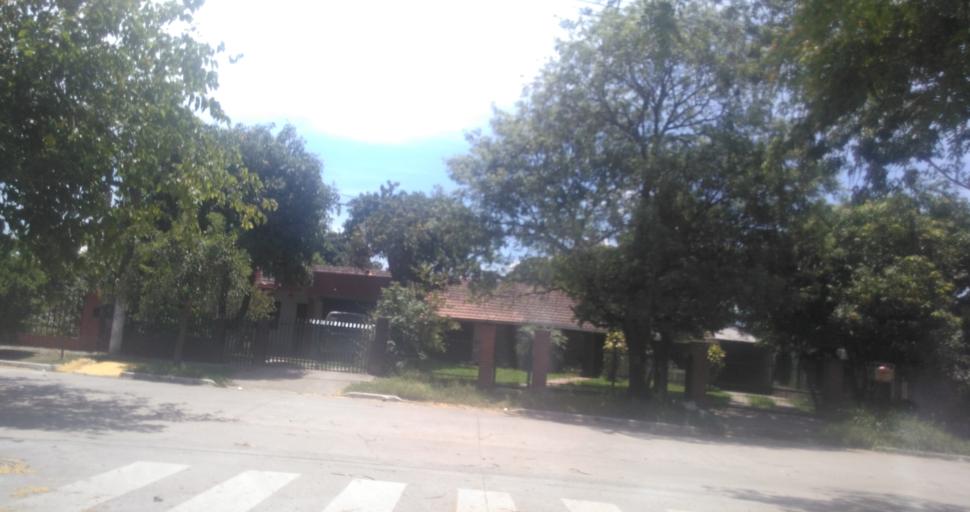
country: AR
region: Chaco
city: Fontana
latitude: -27.4151
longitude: -59.0331
